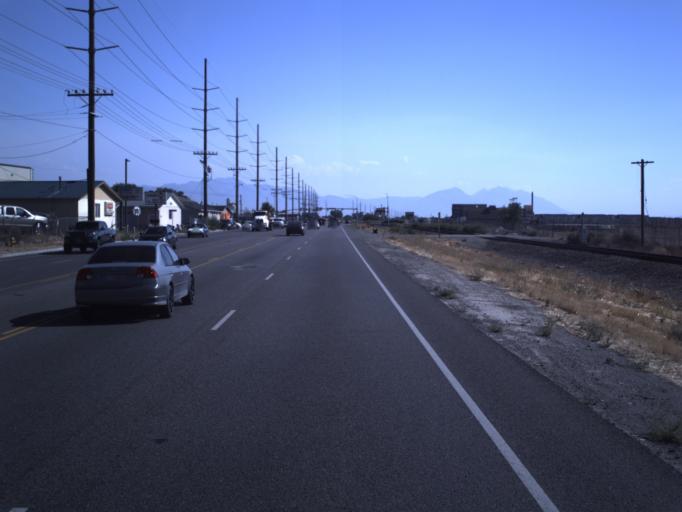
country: US
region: Utah
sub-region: Utah County
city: Lindon
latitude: 40.3154
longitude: -111.7354
